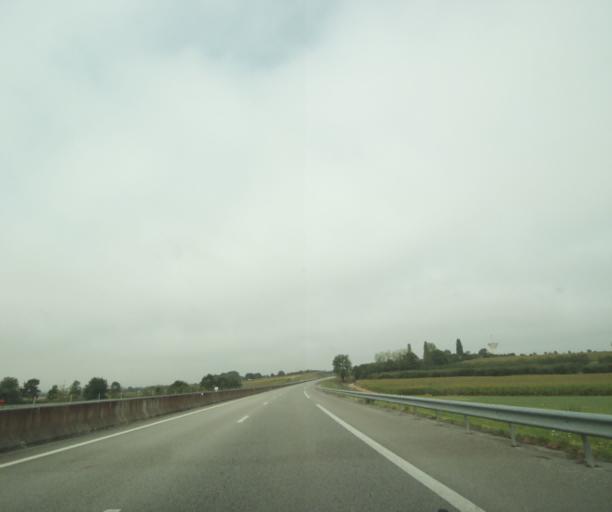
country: FR
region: Lower Normandy
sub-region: Departement de l'Orne
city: Sees
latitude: 48.6432
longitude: 0.1453
